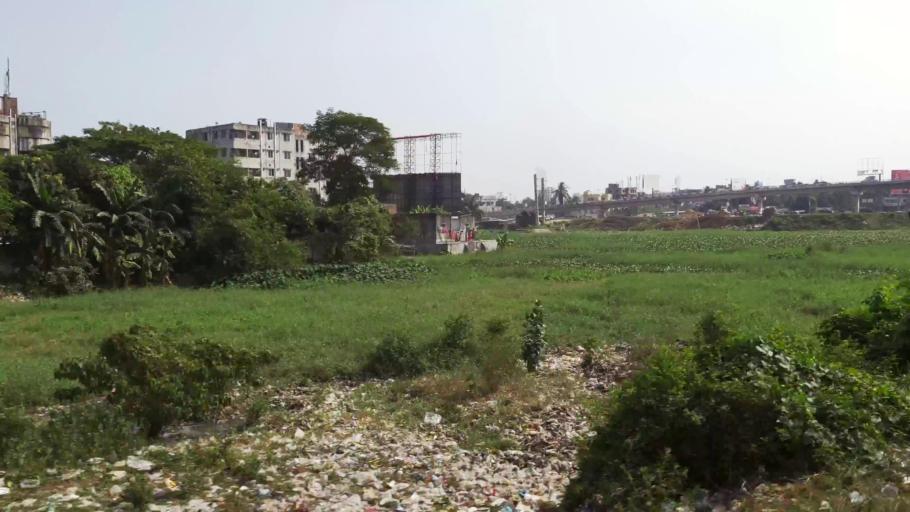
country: BD
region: Dhaka
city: Tungi
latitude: 23.8837
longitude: 90.4066
